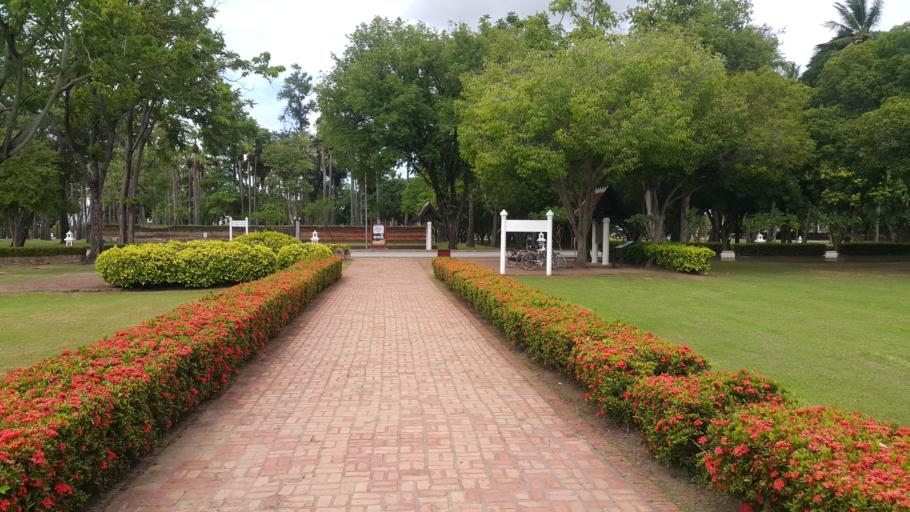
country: TH
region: Sukhothai
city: Ban Na
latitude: 17.0167
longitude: 99.7048
